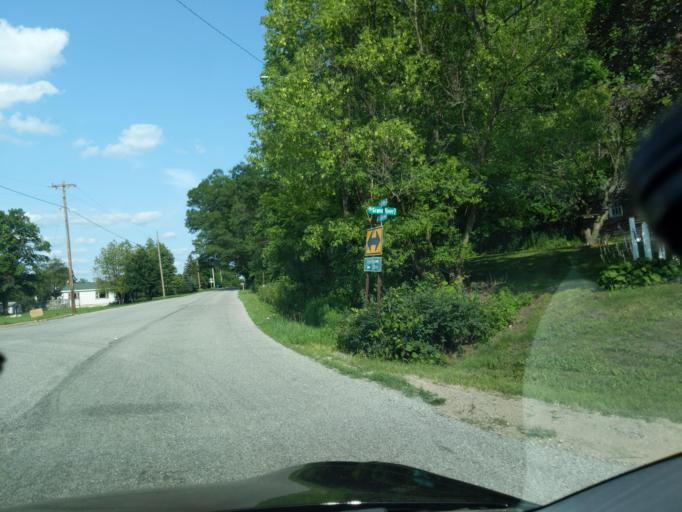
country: US
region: Michigan
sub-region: Kent County
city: Lowell
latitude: 42.9261
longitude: -85.3318
